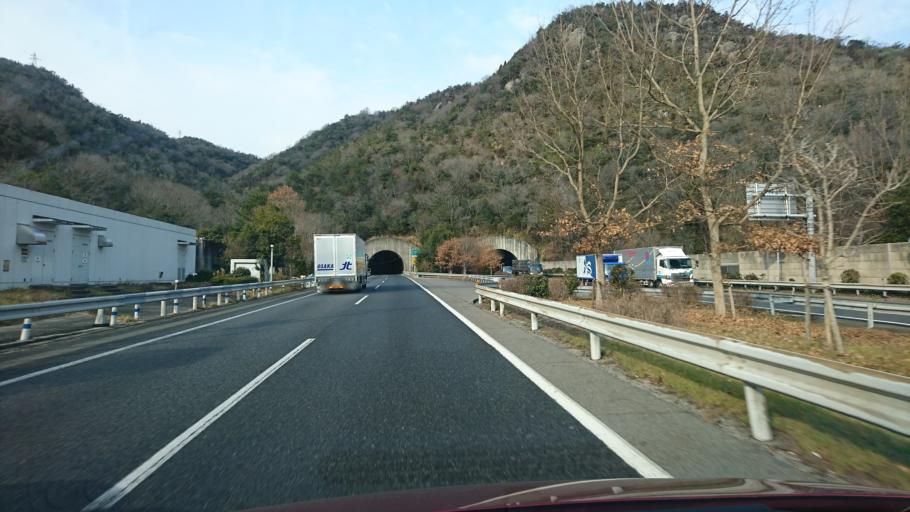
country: JP
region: Hyogo
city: Kariya
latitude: 34.7876
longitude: 134.1506
